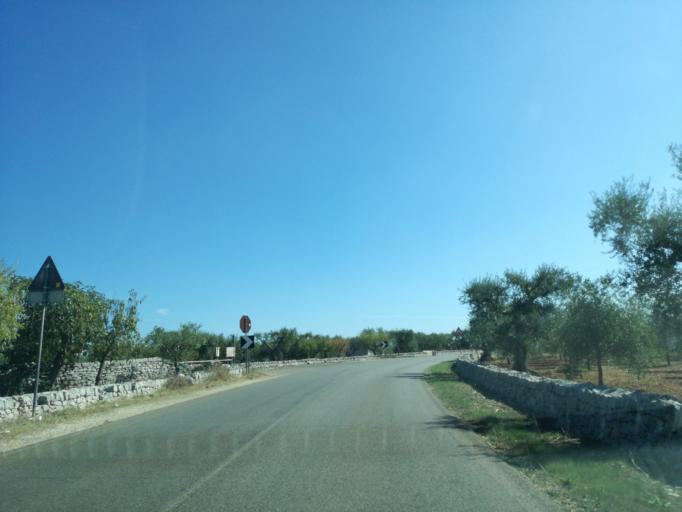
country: IT
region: Apulia
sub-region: Provincia di Bari
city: Castellana
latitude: 40.8825
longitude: 17.1377
